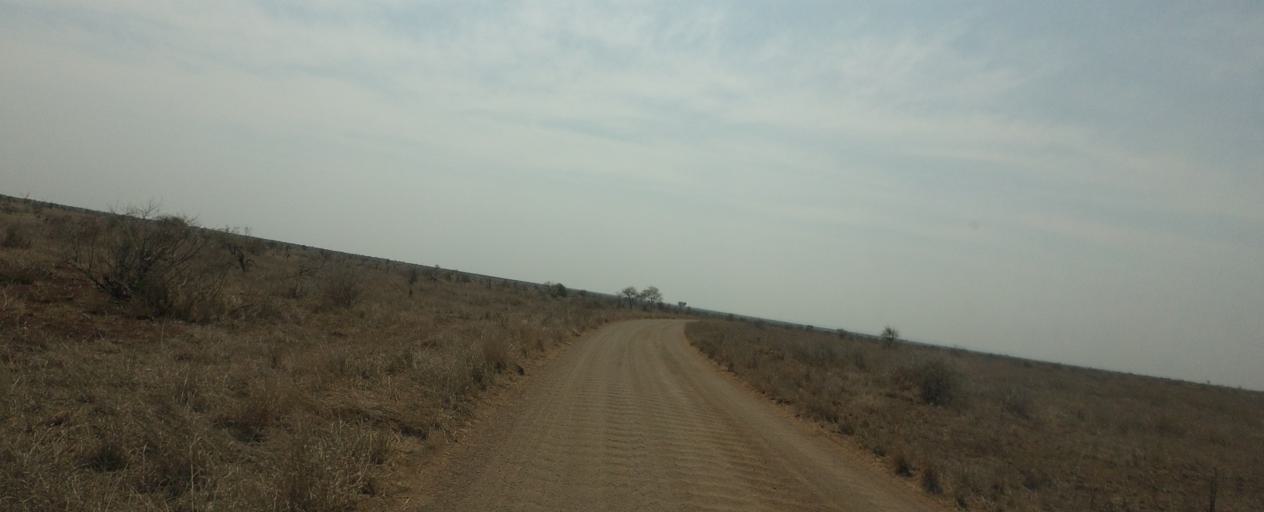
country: ZA
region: Limpopo
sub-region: Mopani District Municipality
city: Phalaborwa
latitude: -24.2543
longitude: 31.6950
